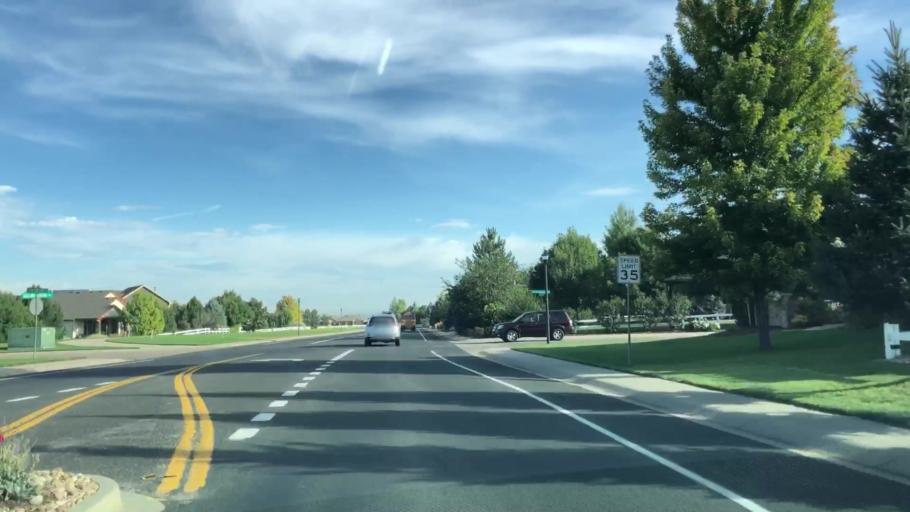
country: US
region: Colorado
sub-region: Weld County
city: Windsor
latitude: 40.4650
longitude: -104.9769
